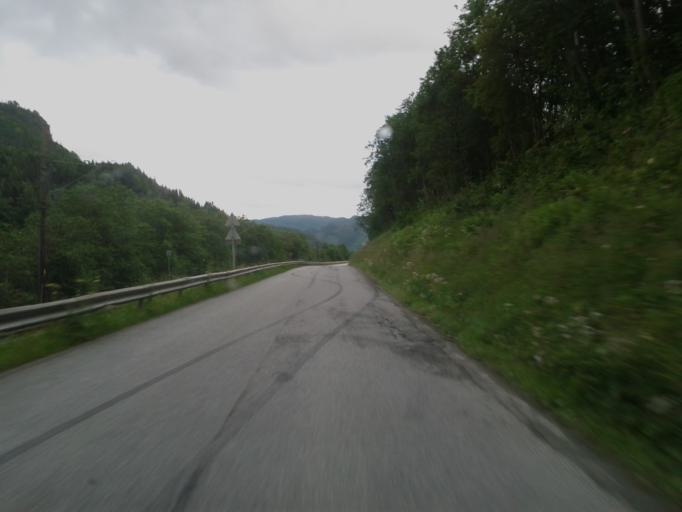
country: NO
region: Sor-Trondelag
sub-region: Midtre Gauldal
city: Storen
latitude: 63.0643
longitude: 10.2872
